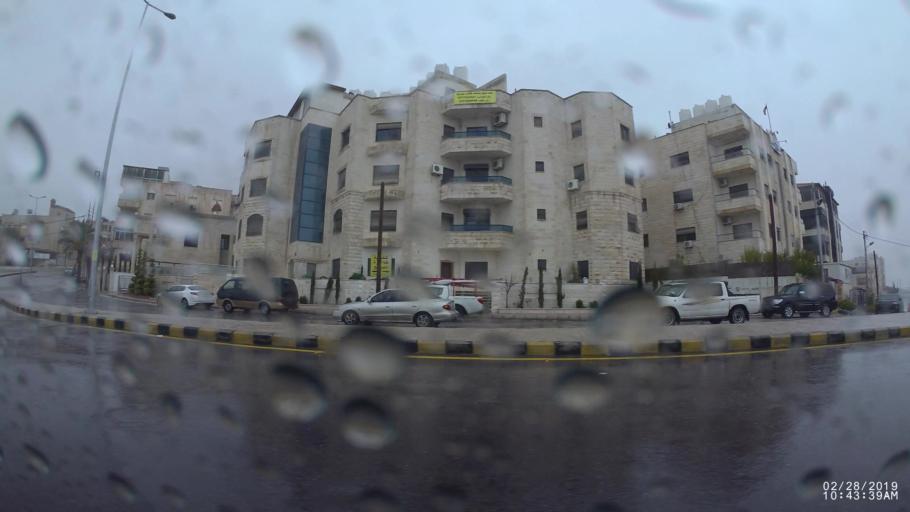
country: JO
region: Amman
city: Al Jubayhah
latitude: 32.0164
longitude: 35.8895
